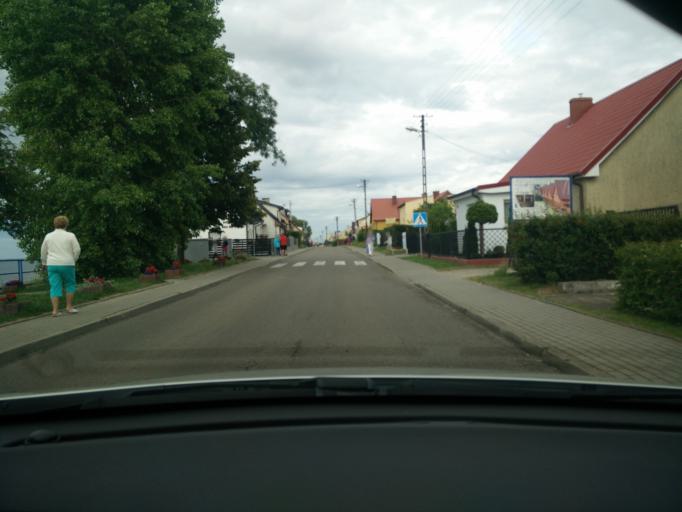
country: PL
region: Pomeranian Voivodeship
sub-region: Powiat pucki
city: Mosty
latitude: 54.6321
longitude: 18.4992
